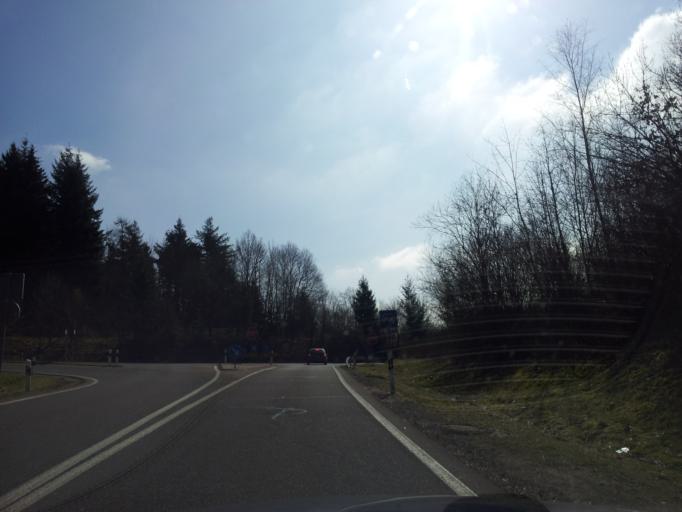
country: DE
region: Rheinland-Pfalz
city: Grosslangenfeld
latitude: 50.2034
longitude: 6.2524
